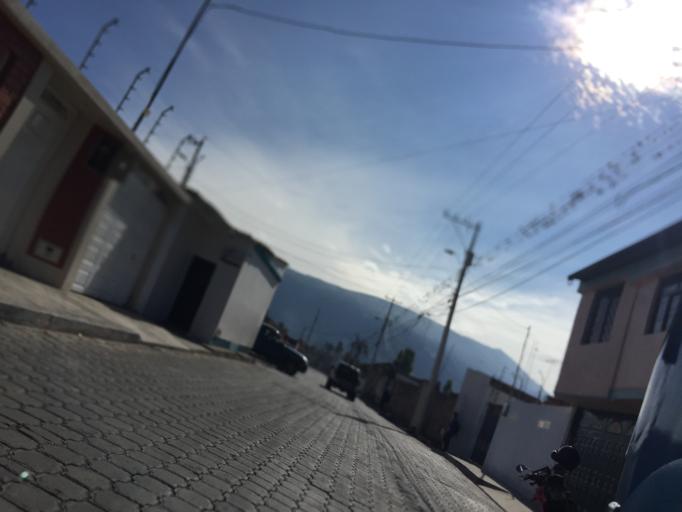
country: EC
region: Imbabura
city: Ibarra
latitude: 0.3170
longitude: -78.1453
